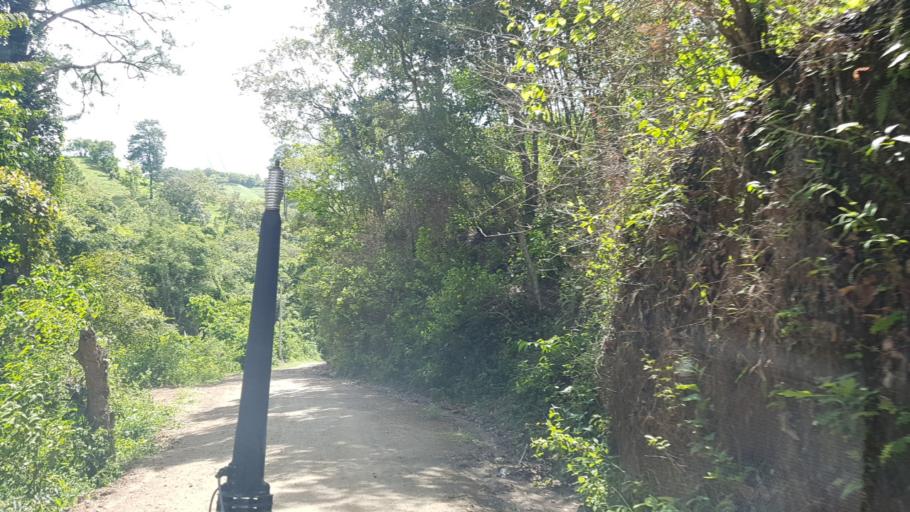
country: NI
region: Nueva Segovia
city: Ciudad Antigua
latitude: 13.6519
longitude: -86.2360
